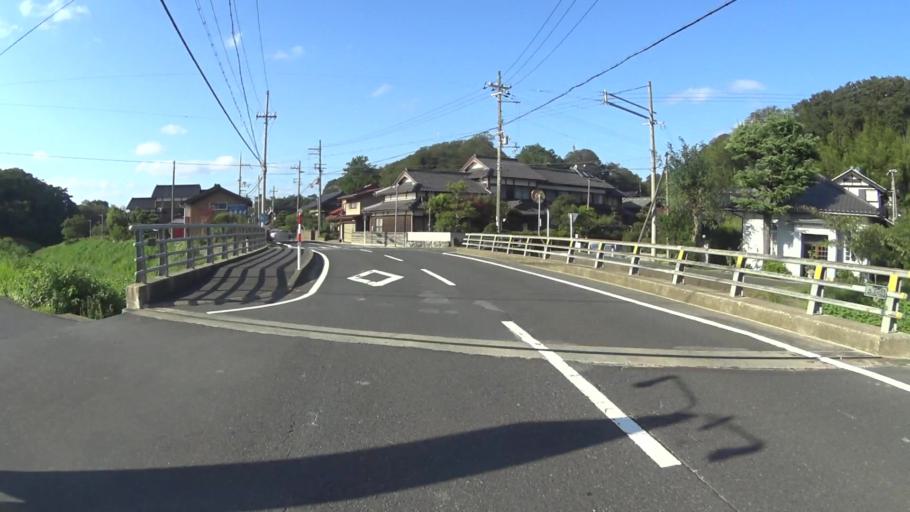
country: JP
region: Hyogo
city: Toyooka
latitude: 35.6533
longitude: 134.9698
